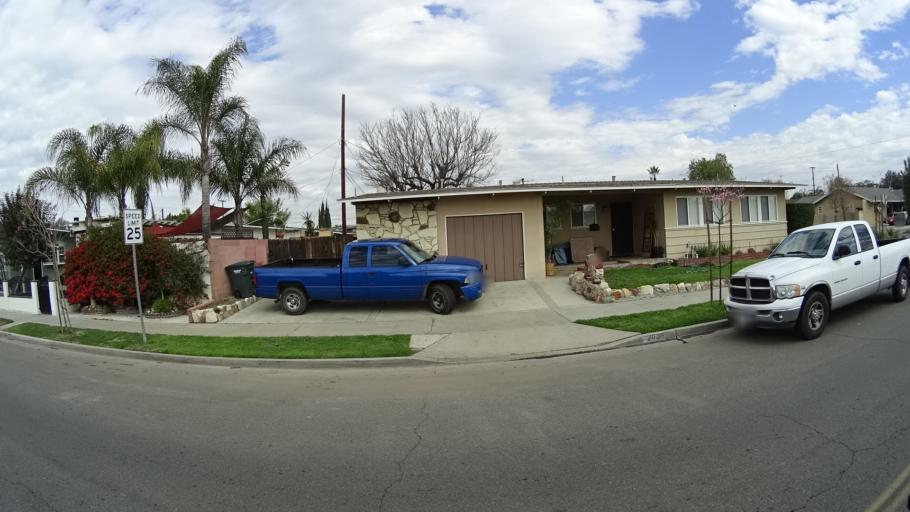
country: US
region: California
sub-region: Orange County
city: Anaheim
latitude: 33.8422
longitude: -117.8853
